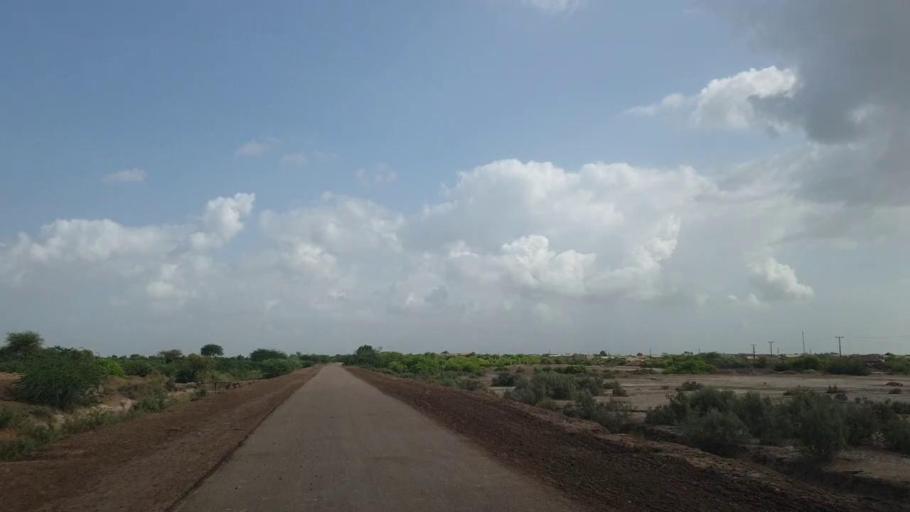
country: PK
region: Sindh
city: Kadhan
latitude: 24.5564
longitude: 69.0638
